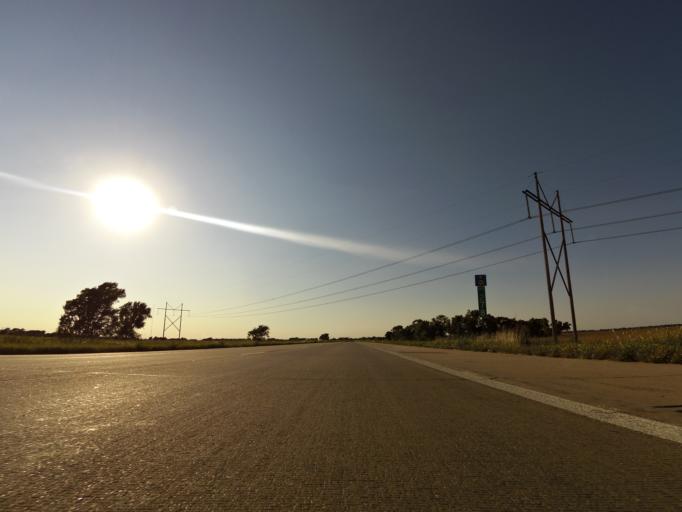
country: US
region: Kansas
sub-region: Sedgwick County
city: Maize
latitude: 37.7965
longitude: -97.4830
